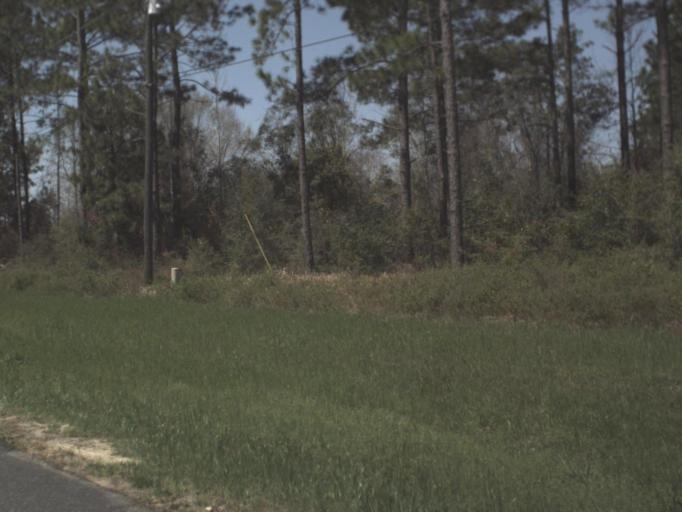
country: US
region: Alabama
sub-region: Geneva County
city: Geneva
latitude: 30.9484
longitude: -85.9372
